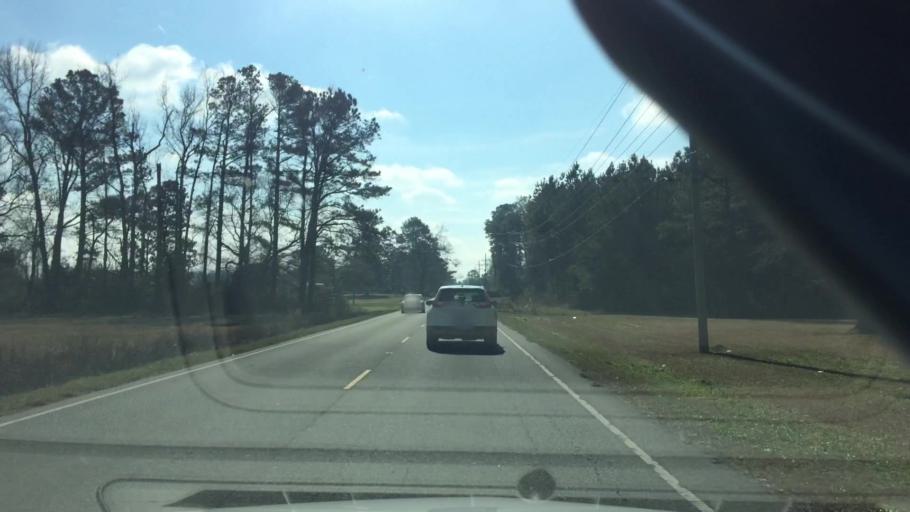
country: US
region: North Carolina
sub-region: Duplin County
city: Beulaville
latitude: 34.8984
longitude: -77.7810
